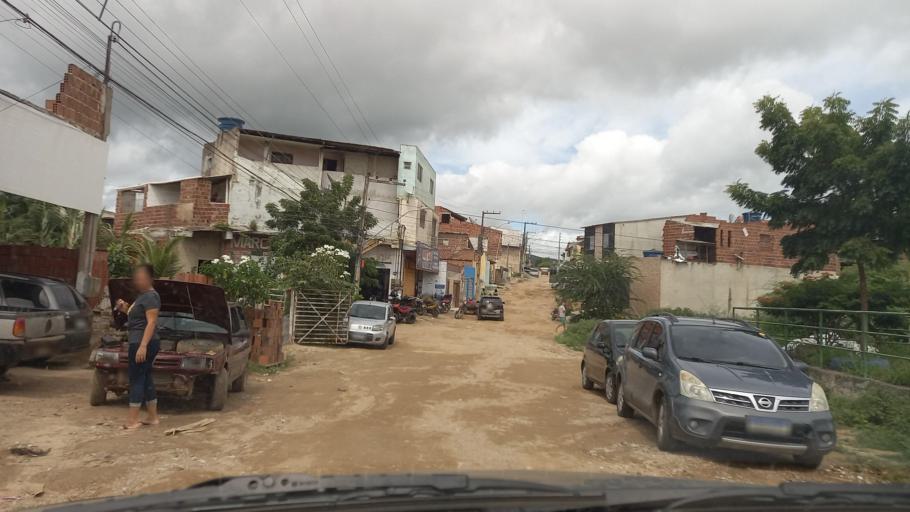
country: ET
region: Oromiya
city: Gore
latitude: 8.1954
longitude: 35.5780
